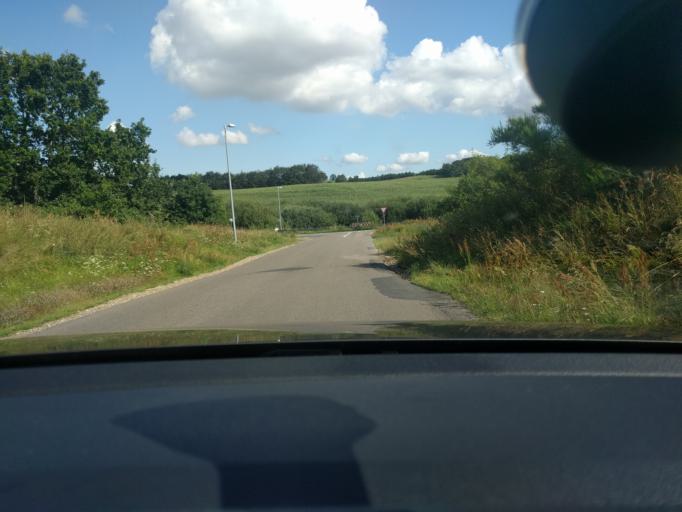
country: DK
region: Central Jutland
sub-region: Viborg Kommune
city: Viborg
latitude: 56.4504
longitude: 9.2878
